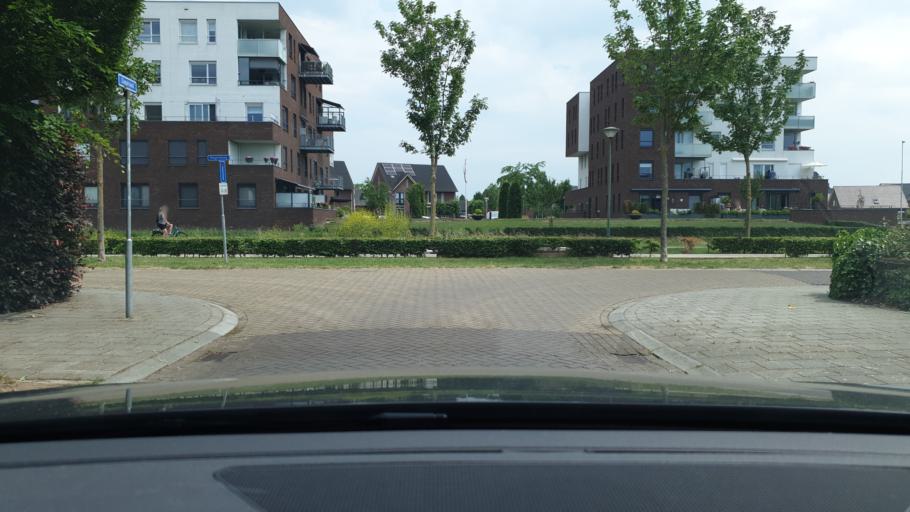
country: NL
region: Gelderland
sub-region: Gemeente Overbetuwe
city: Elst
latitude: 51.9241
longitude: 5.8586
